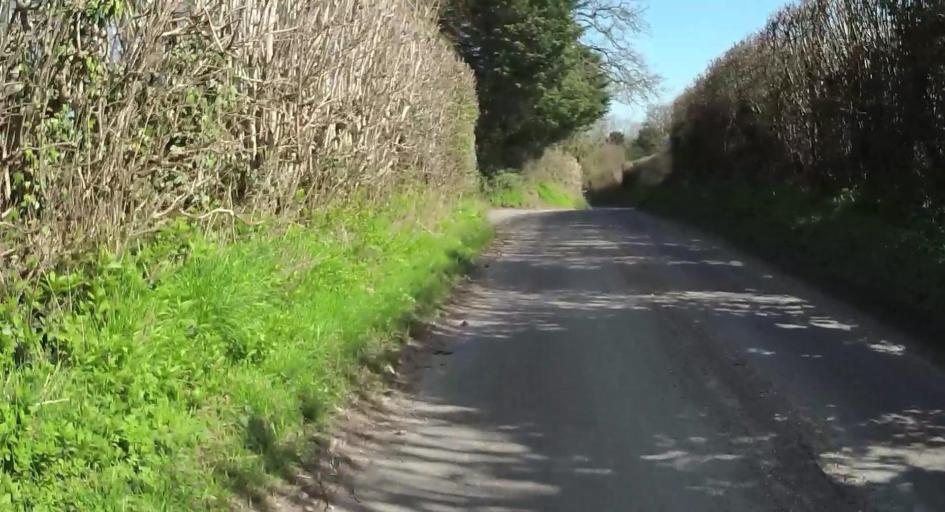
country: GB
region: England
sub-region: Hampshire
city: Highclere
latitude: 51.2795
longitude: -1.4036
